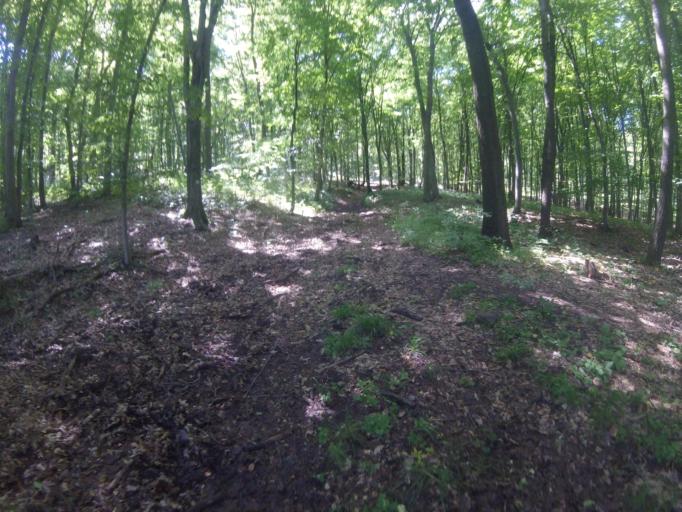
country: HU
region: Nograd
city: Batonyterenye
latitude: 47.9240
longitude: 19.8139
